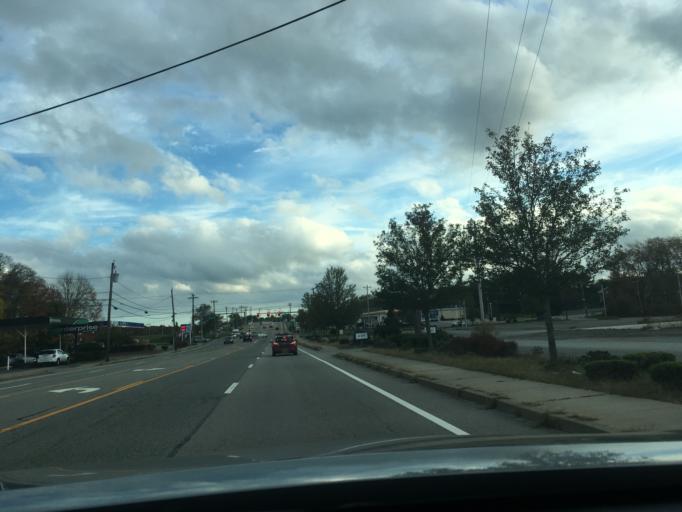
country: US
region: Rhode Island
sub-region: Kent County
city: East Greenwich
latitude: 41.6086
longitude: -71.4563
